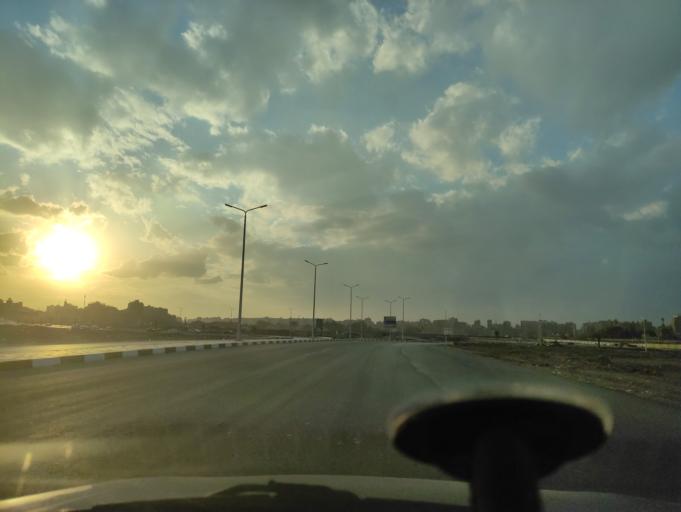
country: EG
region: Muhafazat al Qalyubiyah
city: Al Khankah
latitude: 30.1218
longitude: 31.3625
